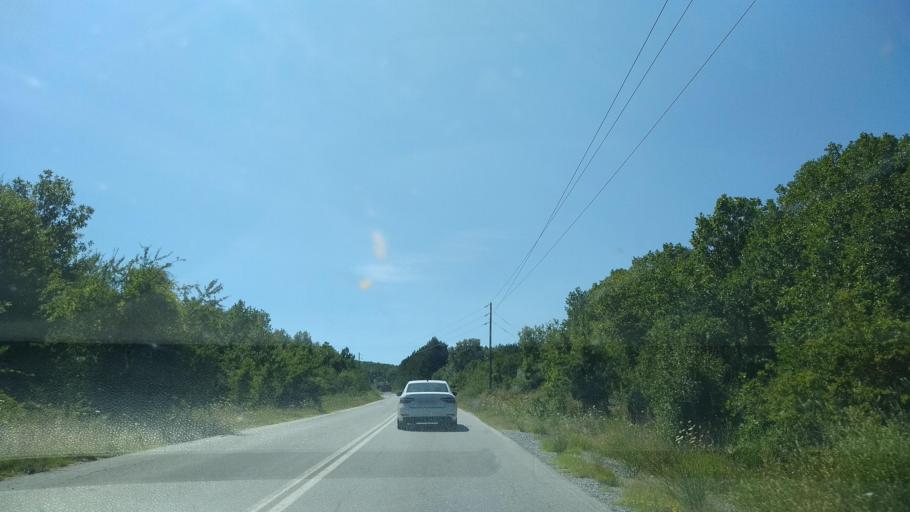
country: GR
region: Central Macedonia
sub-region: Nomos Chalkidikis
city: Palaiochori
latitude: 40.4618
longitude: 23.6534
